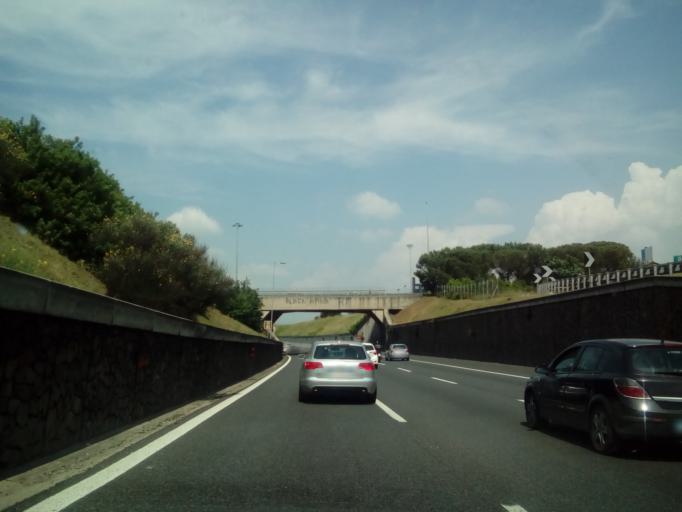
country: IT
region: Latium
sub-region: Citta metropolitana di Roma Capitale
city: Ciampino
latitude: 41.8117
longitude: 12.5716
